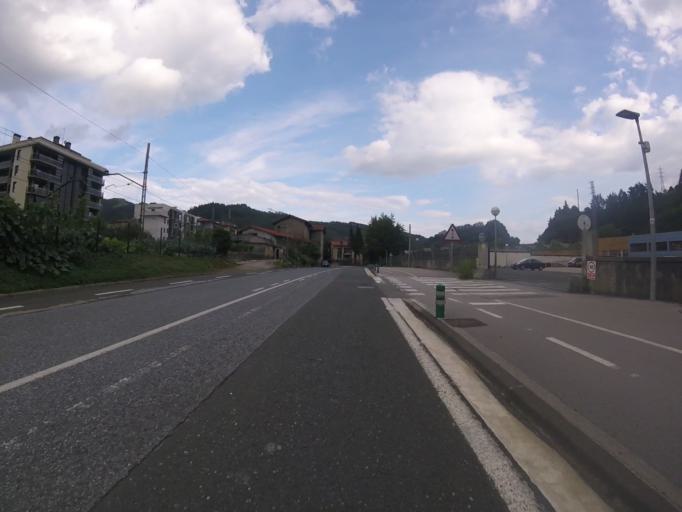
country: ES
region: Basque Country
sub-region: Provincia de Guipuzcoa
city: Anoeta
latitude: 43.1602
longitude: -2.0686
